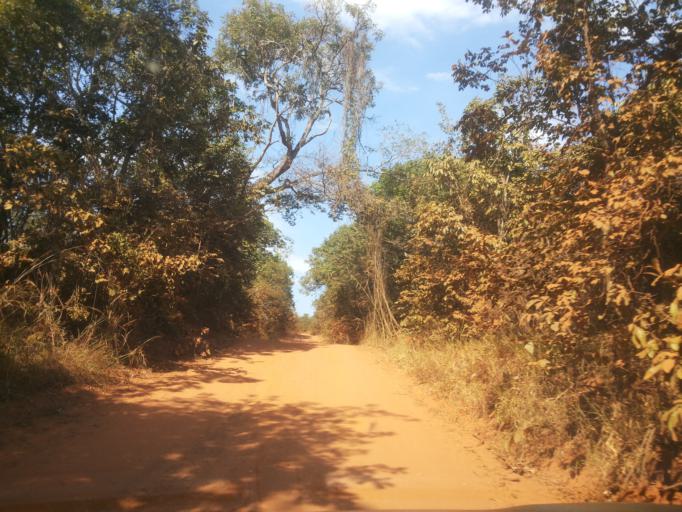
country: BR
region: Minas Gerais
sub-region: Ituiutaba
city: Ituiutaba
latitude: -19.0522
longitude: -49.3639
